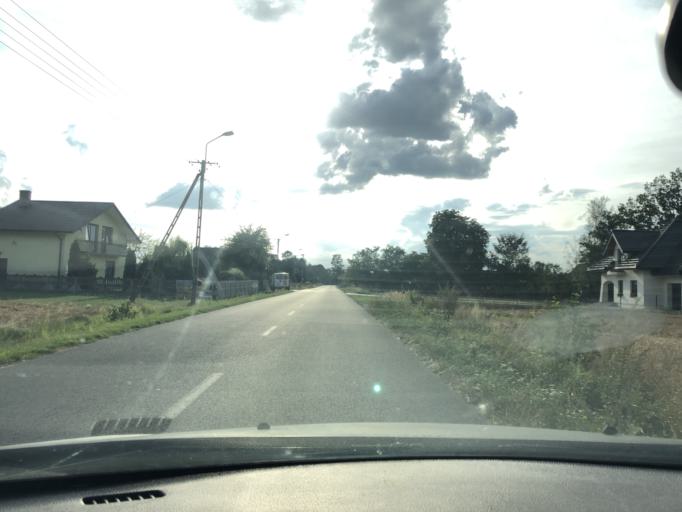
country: PL
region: Lodz Voivodeship
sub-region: Powiat wieruszowski
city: Walichnowy
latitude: 51.2456
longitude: 18.3752
